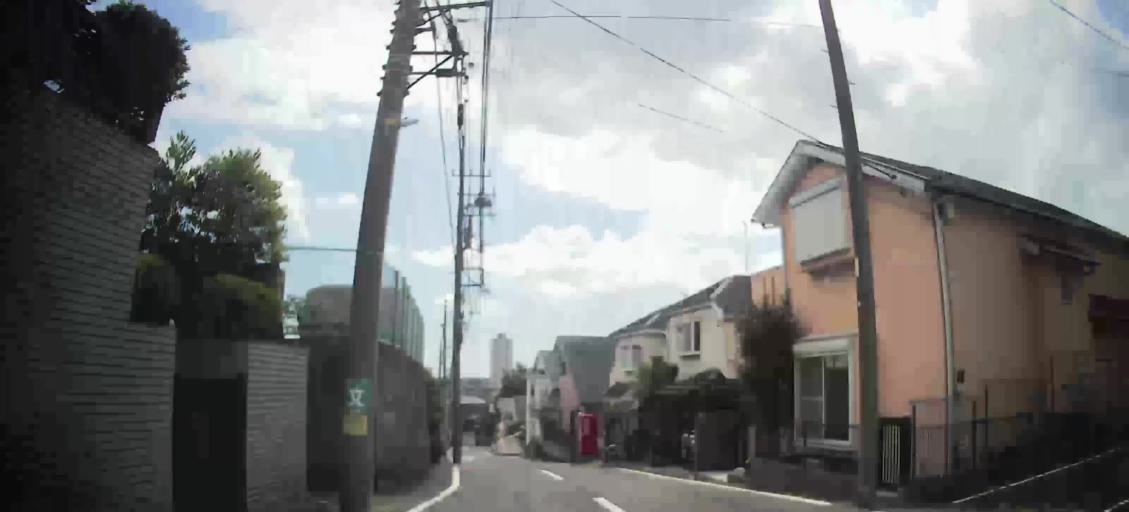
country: JP
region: Kanagawa
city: Yokohama
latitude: 35.4836
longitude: 139.5510
